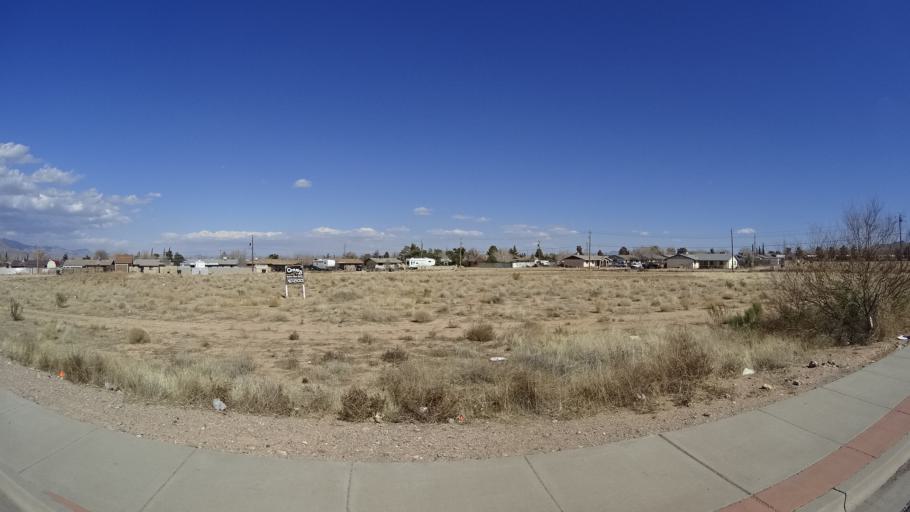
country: US
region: Arizona
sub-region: Mohave County
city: Kingman
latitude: 35.1904
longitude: -114.0147
